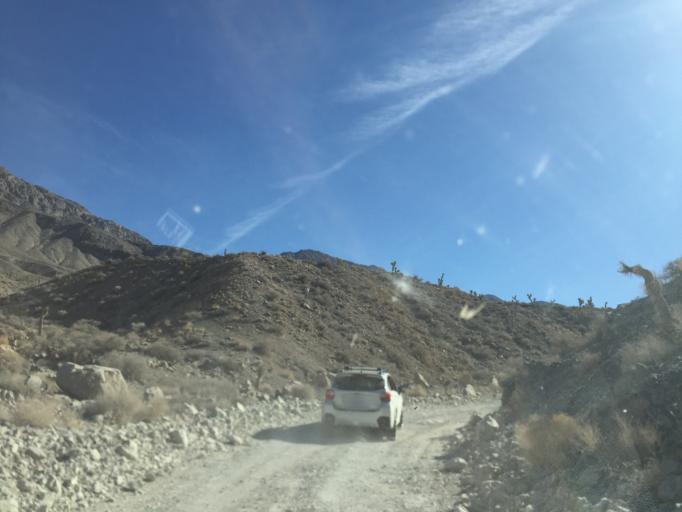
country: US
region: California
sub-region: Inyo County
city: Lone Pine
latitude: 36.8772
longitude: -117.5001
